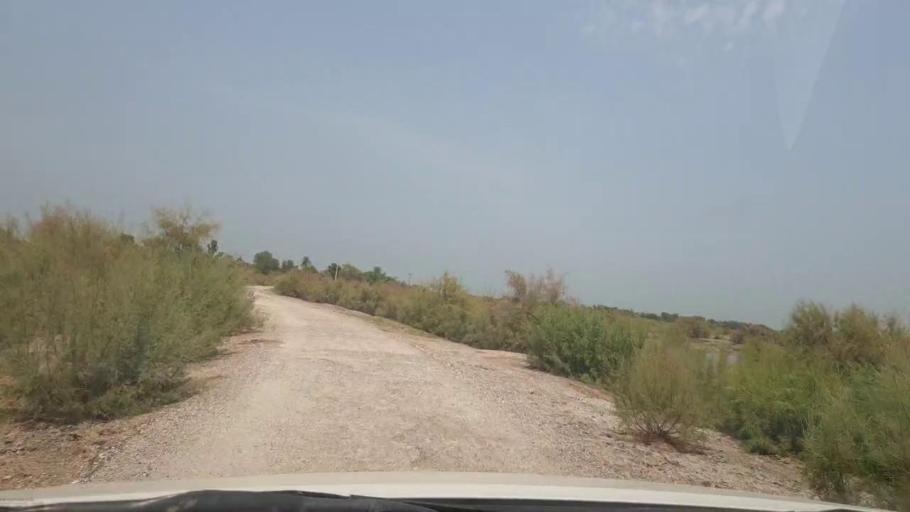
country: PK
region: Sindh
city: Rustam jo Goth
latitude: 28.0567
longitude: 68.7527
